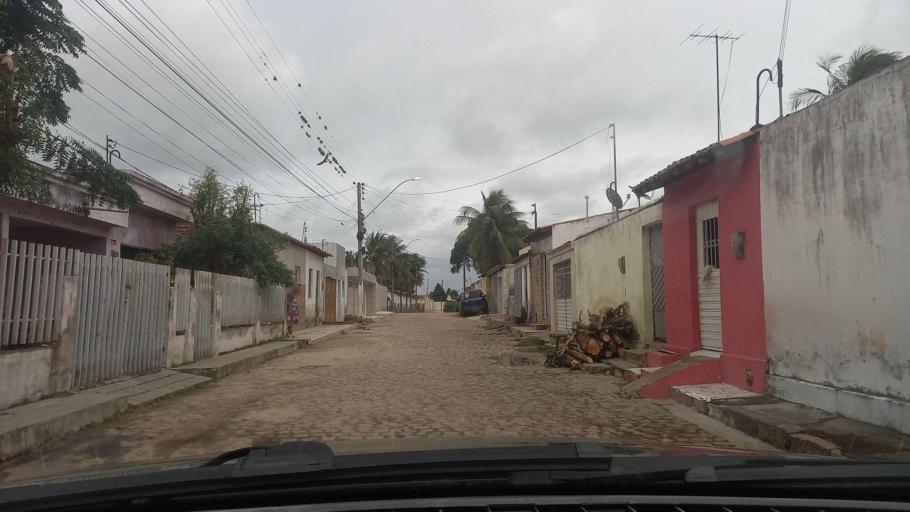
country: BR
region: Alagoas
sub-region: Delmiro Gouveia
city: Delmiro Gouveia
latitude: -9.3872
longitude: -37.9929
